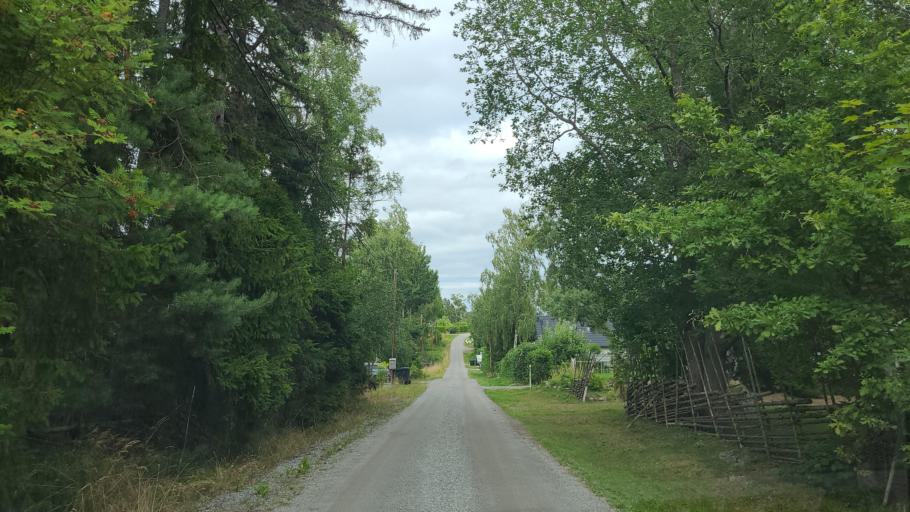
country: SE
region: Uppsala
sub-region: Habo Kommun
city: Balsta
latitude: 59.4770
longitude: 17.5487
